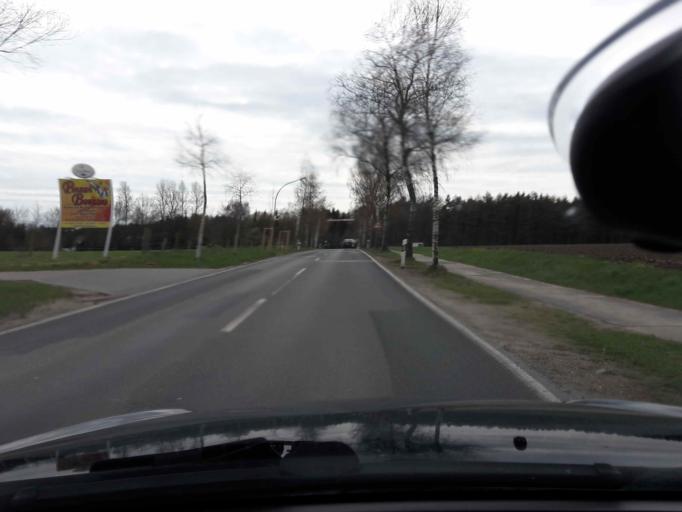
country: DE
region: Lower Saxony
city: Buchholz in der Nordheide
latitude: 53.2977
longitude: 9.8718
